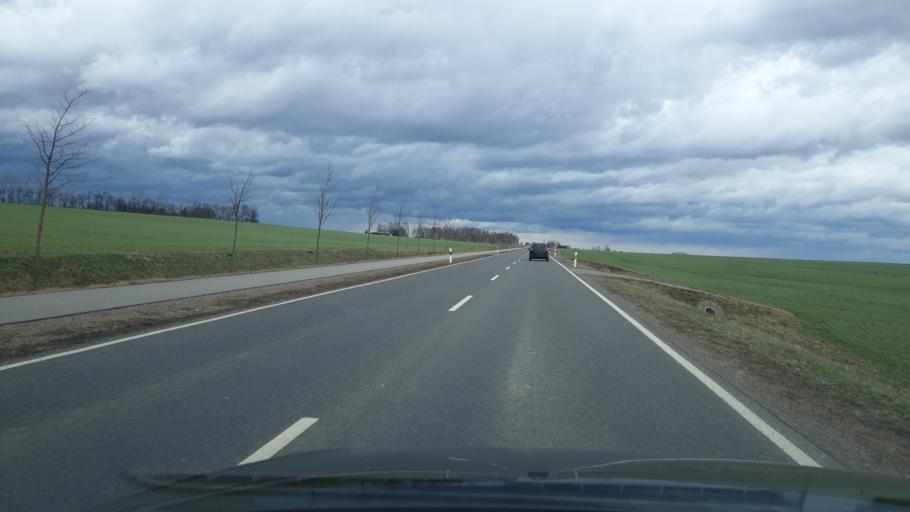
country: DE
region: Saxony
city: Claussnitz
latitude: 50.9490
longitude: 12.9076
